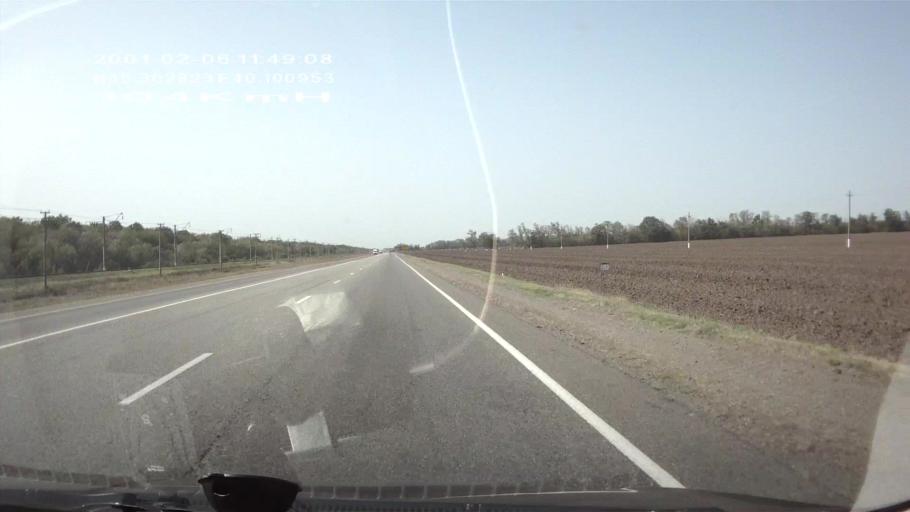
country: RU
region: Krasnodarskiy
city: Tbilisskaya
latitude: 45.3631
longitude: 40.0997
